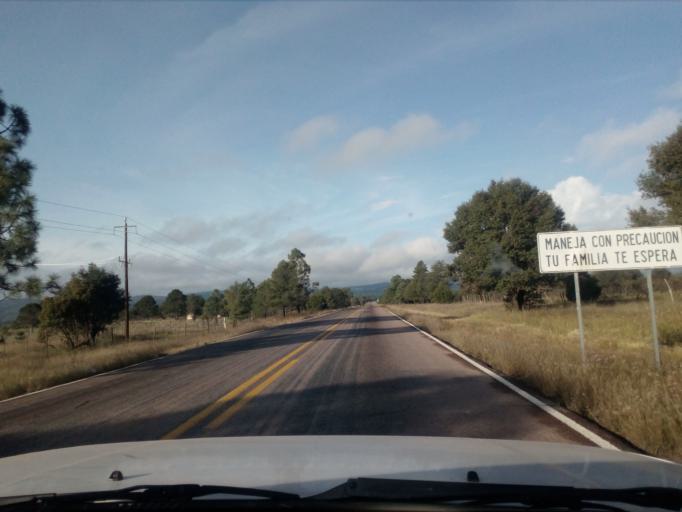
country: MX
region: Durango
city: Victoria de Durango
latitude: 23.9317
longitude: -104.9174
